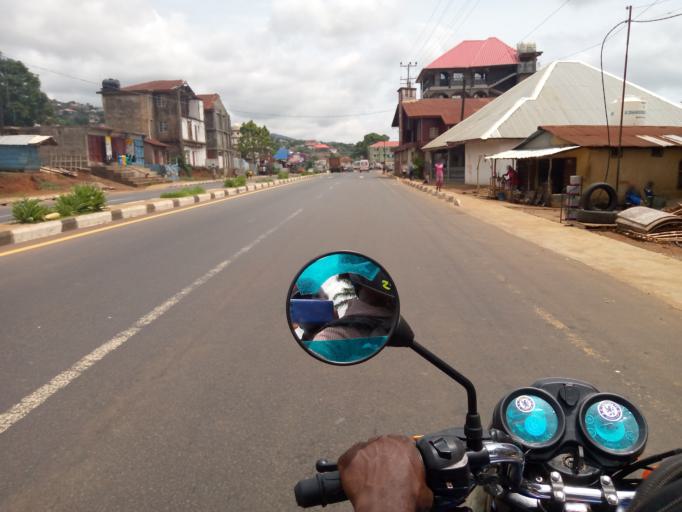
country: SL
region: Western Area
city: Hastings
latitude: 8.4150
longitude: -13.1507
